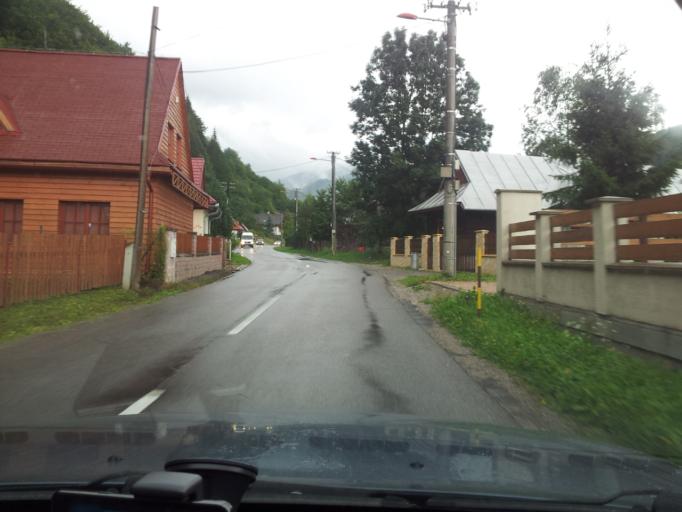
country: SK
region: Banskobystricky
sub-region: Okres Banska Bystrica
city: Brezno
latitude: 48.8557
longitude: 19.6336
